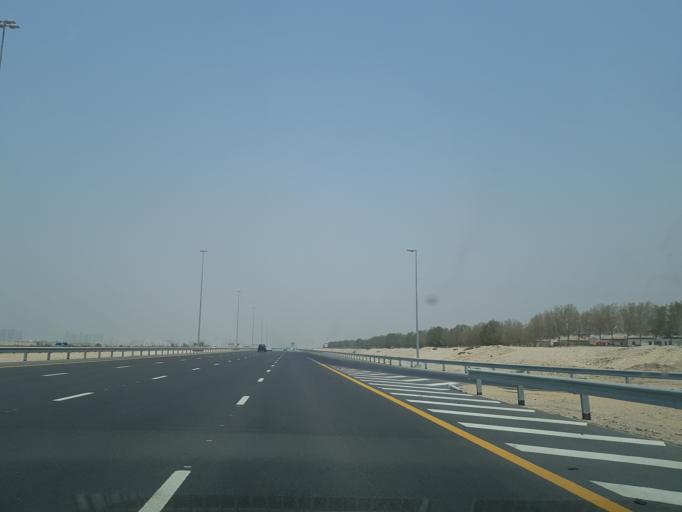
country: AE
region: Dubai
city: Dubai
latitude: 25.0860
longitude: 55.3489
